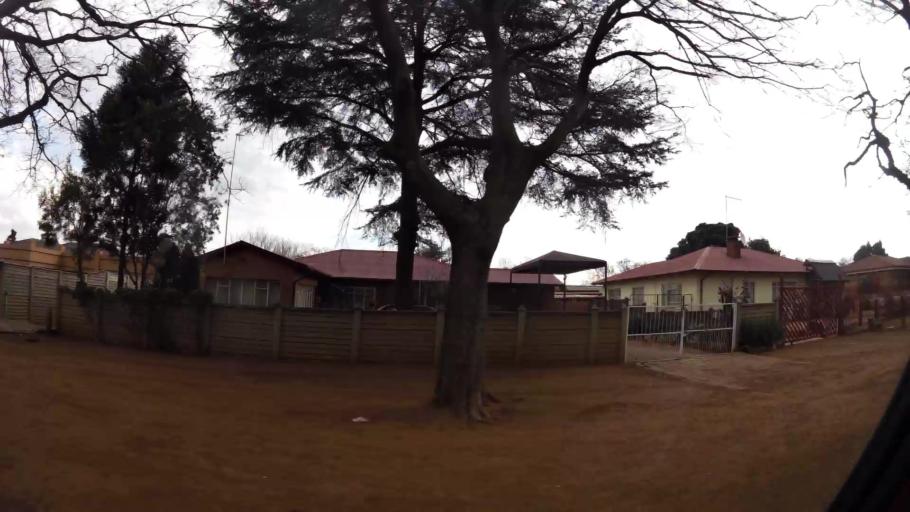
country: ZA
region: Gauteng
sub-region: Sedibeng District Municipality
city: Vanderbijlpark
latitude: -26.7003
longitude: 27.8229
